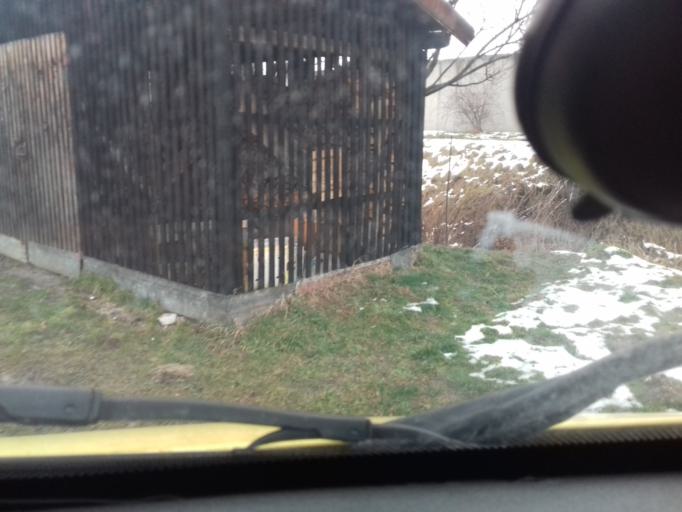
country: BA
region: Federation of Bosnia and Herzegovina
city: Vitez
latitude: 44.1543
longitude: 17.7870
